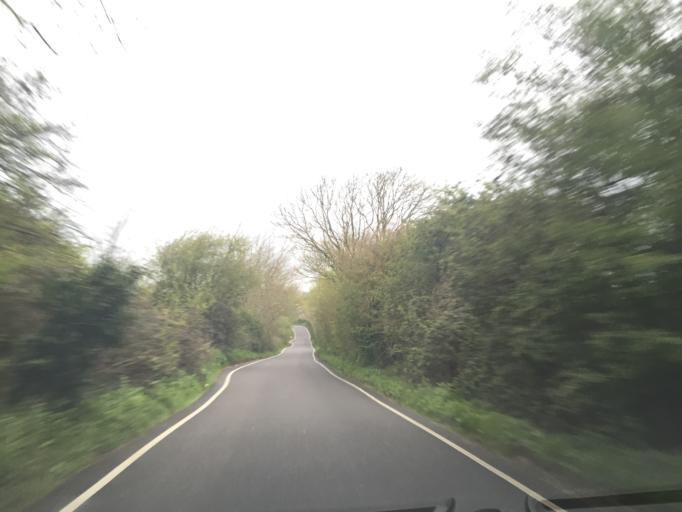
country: GB
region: England
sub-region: Essex
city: Epping
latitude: 51.7355
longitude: 0.1116
